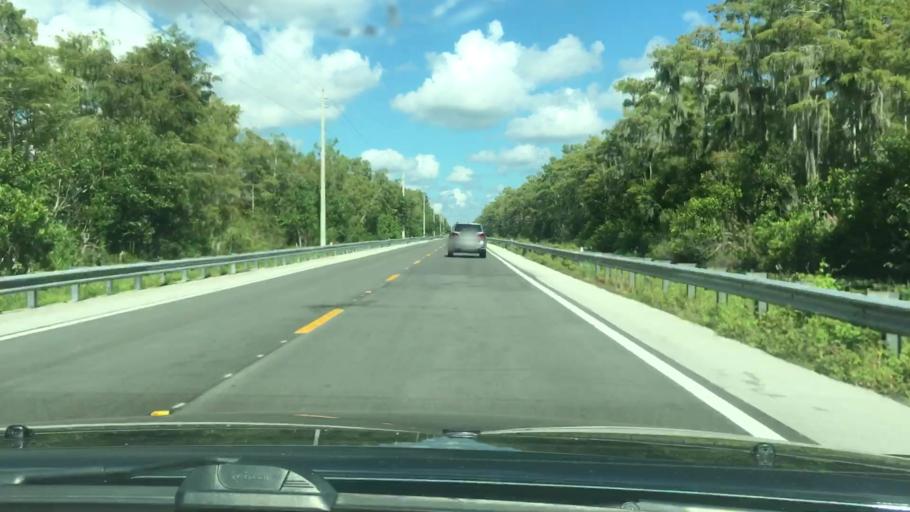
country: US
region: Florida
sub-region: Miami-Dade County
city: Kendall West
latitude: 25.7988
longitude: -80.8662
